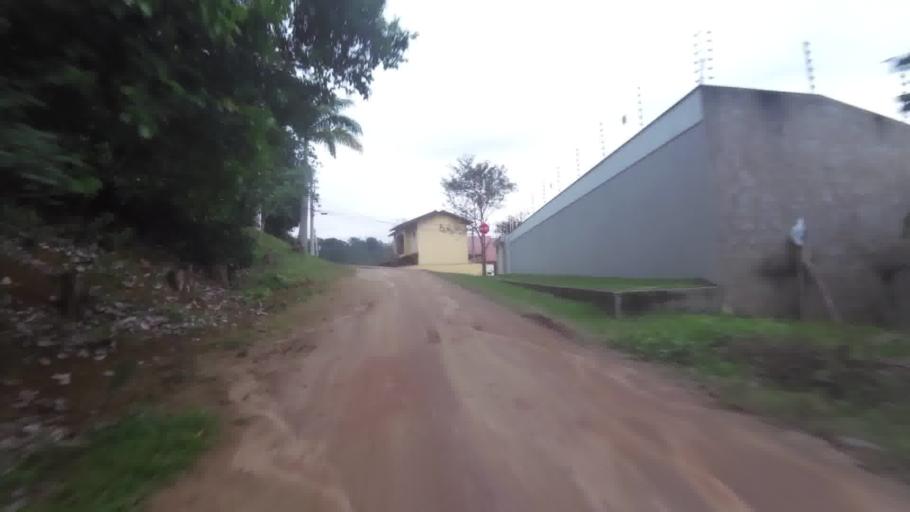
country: BR
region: Espirito Santo
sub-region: Iconha
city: Iconha
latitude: -20.7879
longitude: -40.8143
